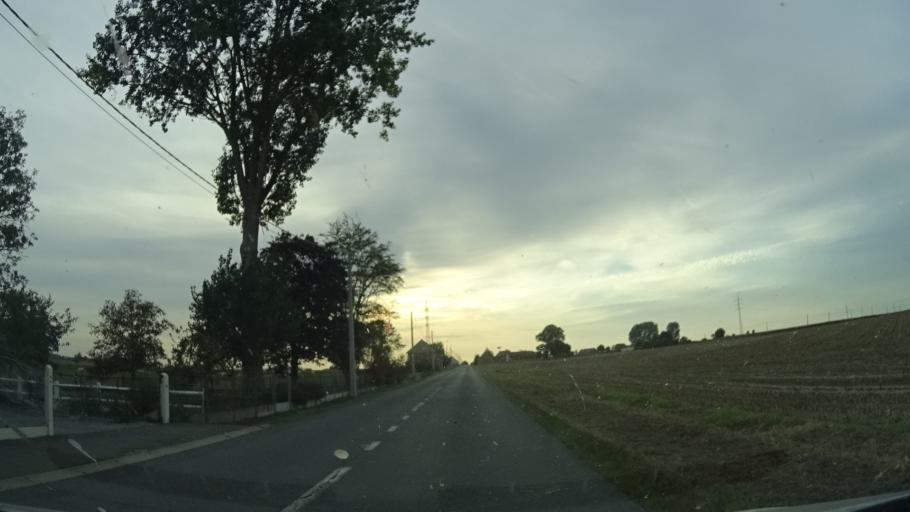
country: BE
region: Wallonia
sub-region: Province du Hainaut
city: Frasnes-lez-Buissenal
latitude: 50.6550
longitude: 3.5787
